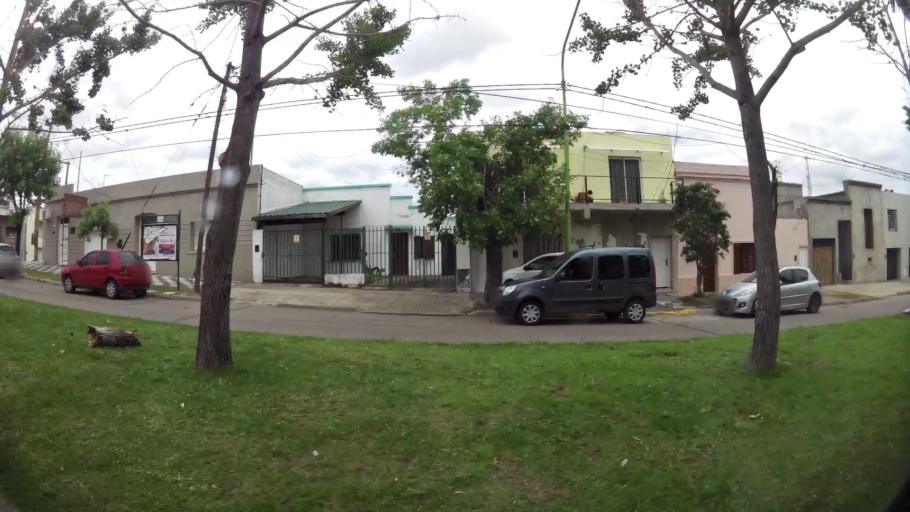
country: AR
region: Buenos Aires
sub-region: Partido de Campana
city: Campana
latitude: -34.1635
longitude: -58.9543
